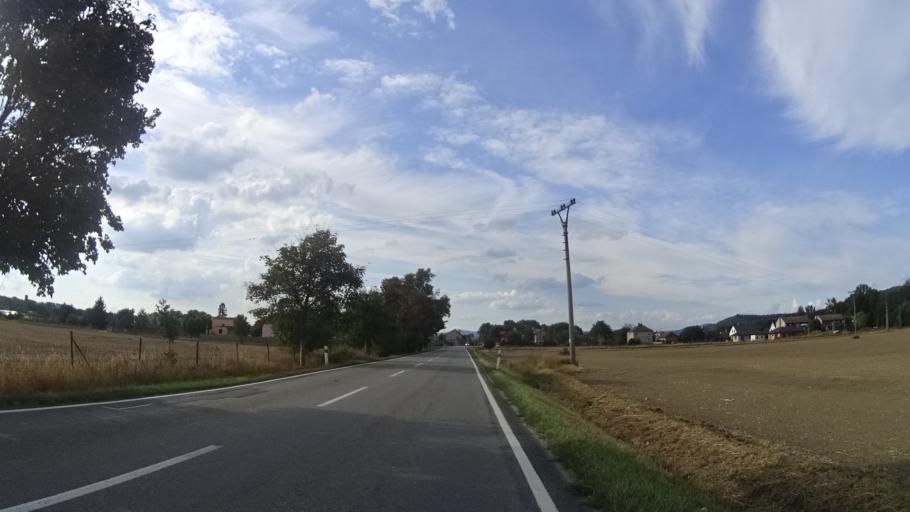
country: CZ
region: Olomoucky
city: Lestina
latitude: 49.8668
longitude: 16.9349
